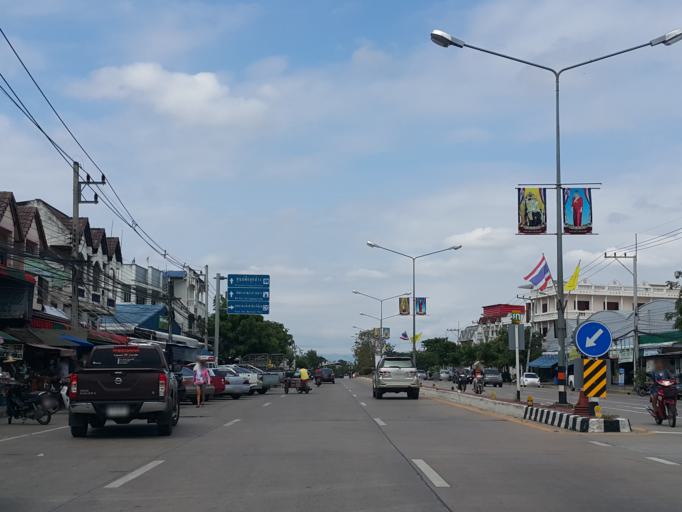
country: TH
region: Lampang
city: Lampang
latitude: 18.3087
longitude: 99.4669
